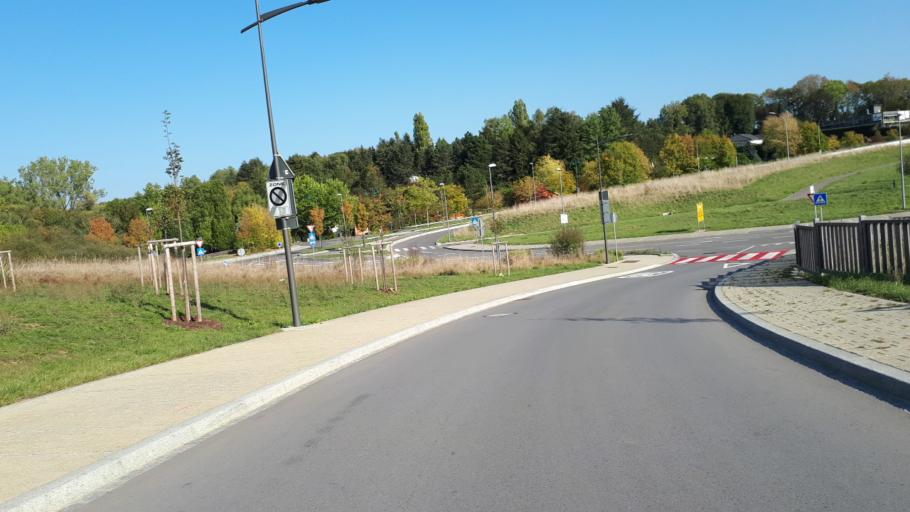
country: LU
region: Luxembourg
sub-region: Canton de Capellen
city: Mamer
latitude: 49.6233
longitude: 6.0356
